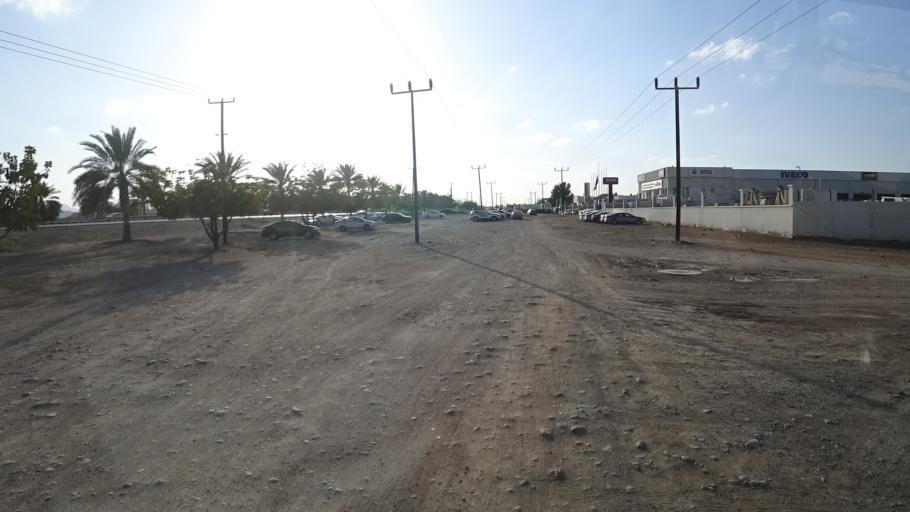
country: OM
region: Muhafazat Masqat
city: As Sib al Jadidah
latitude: 23.5901
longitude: 58.2317
